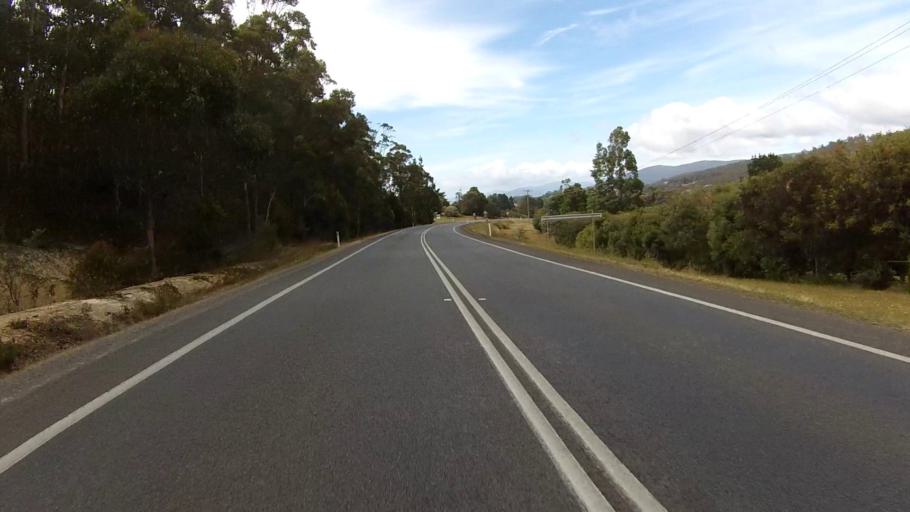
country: AU
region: Tasmania
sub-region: Kingborough
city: Kettering
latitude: -43.1136
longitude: 147.2446
